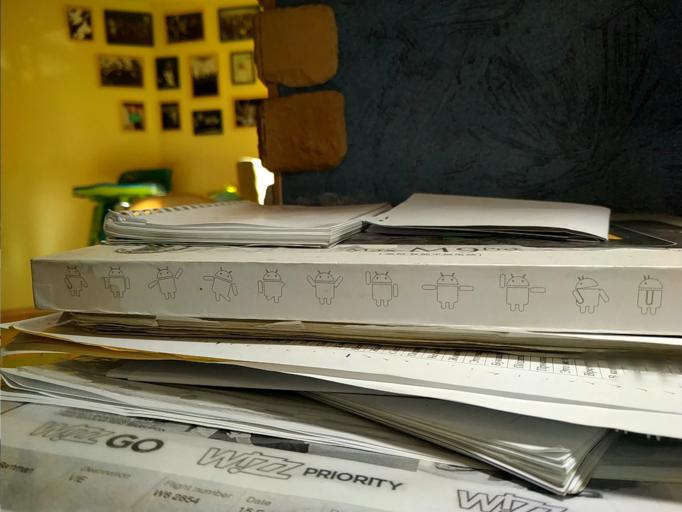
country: RU
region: Novgorod
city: Poddor'ye
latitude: 57.5143
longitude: 30.9260
